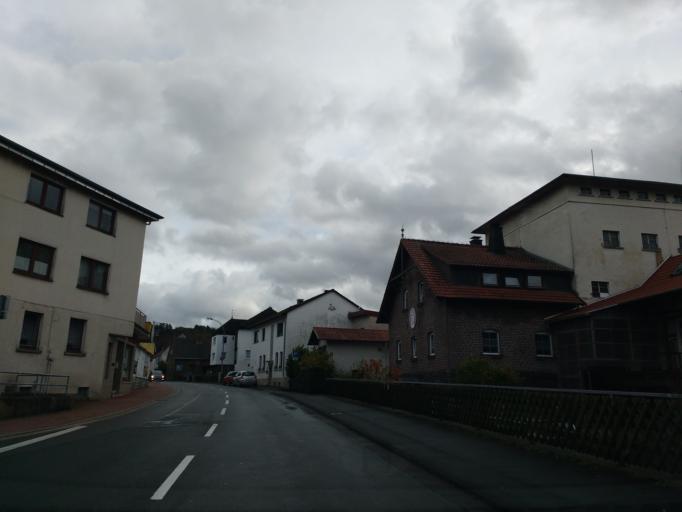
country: DE
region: Hesse
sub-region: Regierungsbezirk Kassel
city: Vohl
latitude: 51.1840
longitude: 8.8938
